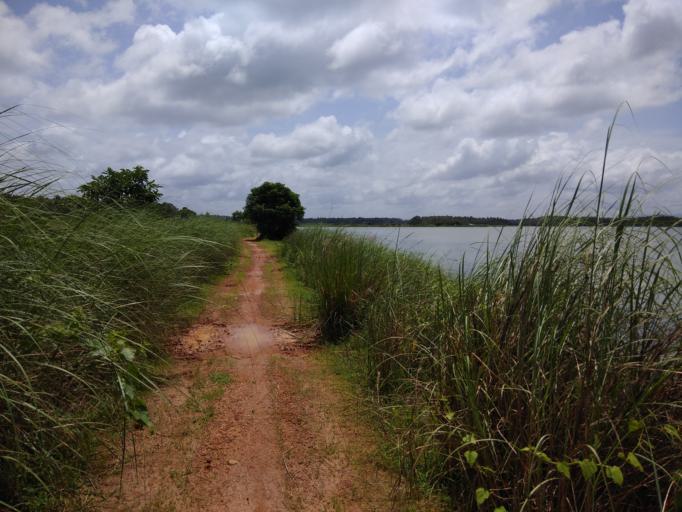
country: IN
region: Kerala
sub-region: Thrissur District
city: Avanoor
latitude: 10.5657
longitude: 76.1355
